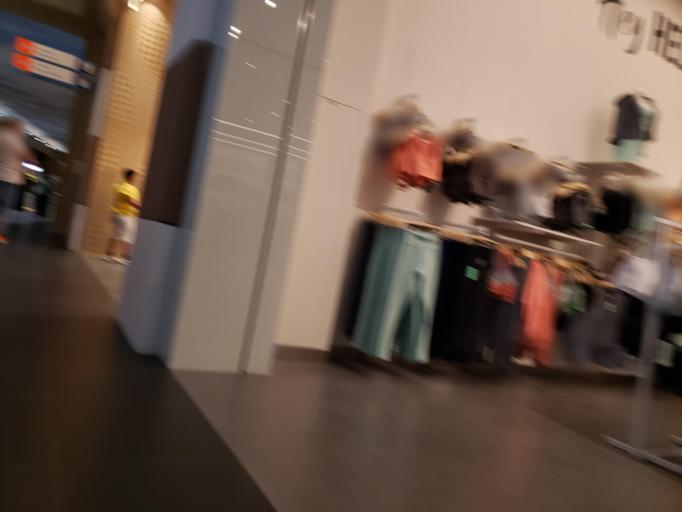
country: AE
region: Dubai
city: Dubai
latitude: 25.0446
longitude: 55.1191
